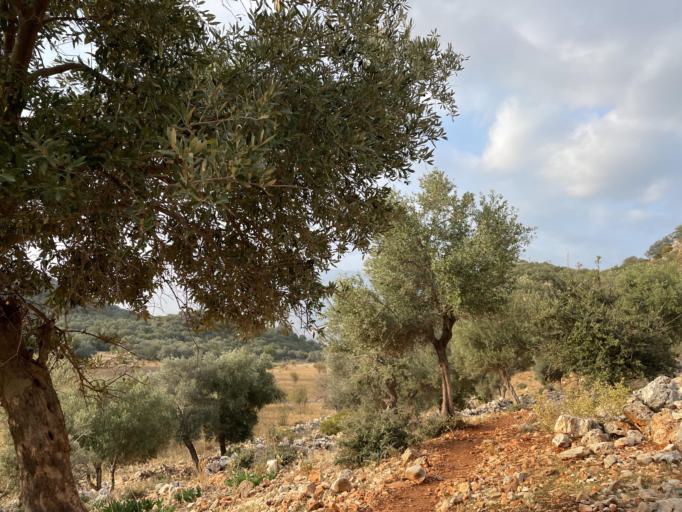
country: TR
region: Antalya
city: Kas
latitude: 36.1675
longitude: 29.6534
